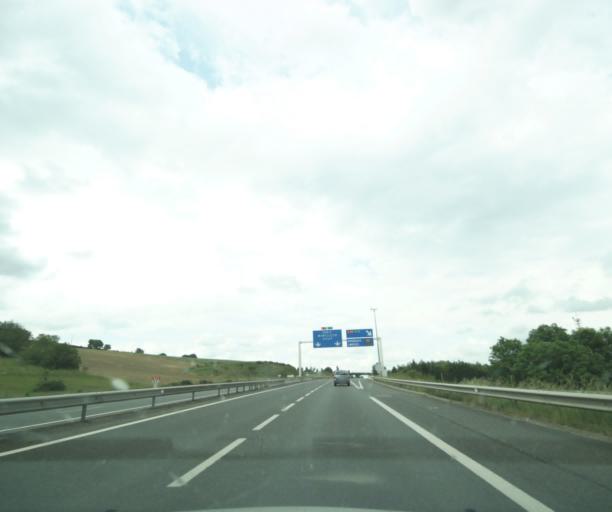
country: FR
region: Auvergne
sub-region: Departement du Puy-de-Dome
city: Combronde
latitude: 45.9681
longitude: 3.1002
